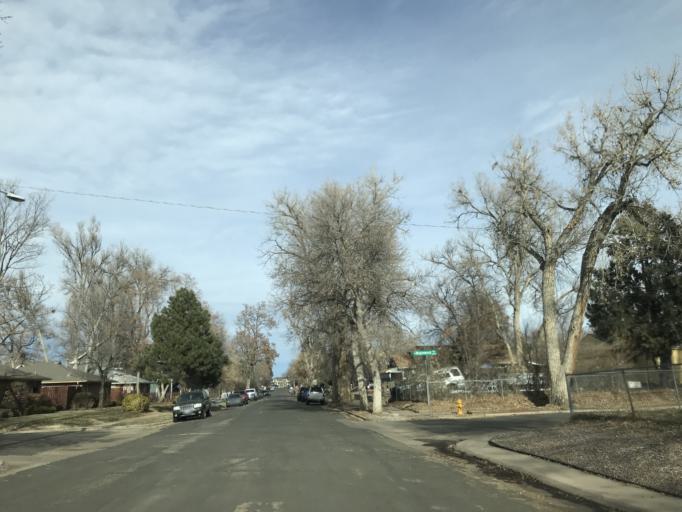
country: US
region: Colorado
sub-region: Arapahoe County
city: Littleton
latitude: 39.6058
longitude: -105.0140
